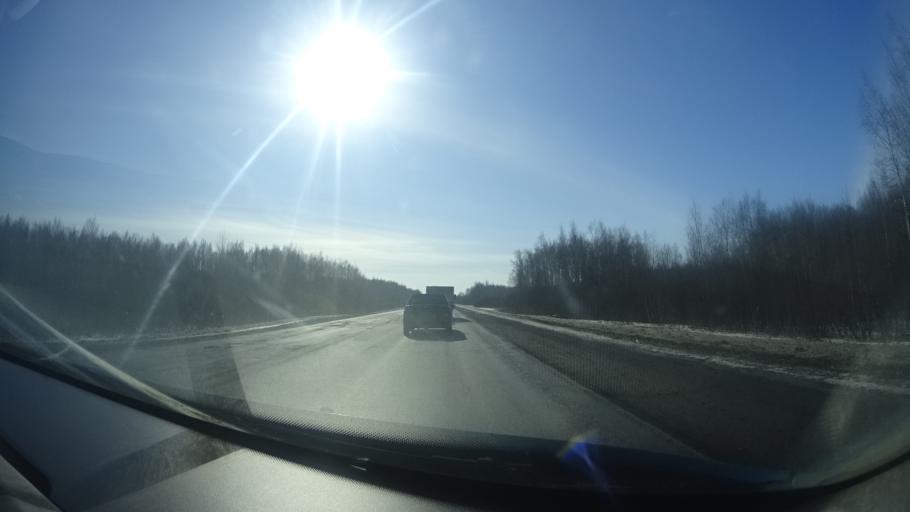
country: RU
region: Bashkortostan
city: Mikhaylovka
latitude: 54.9054
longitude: 55.7293
